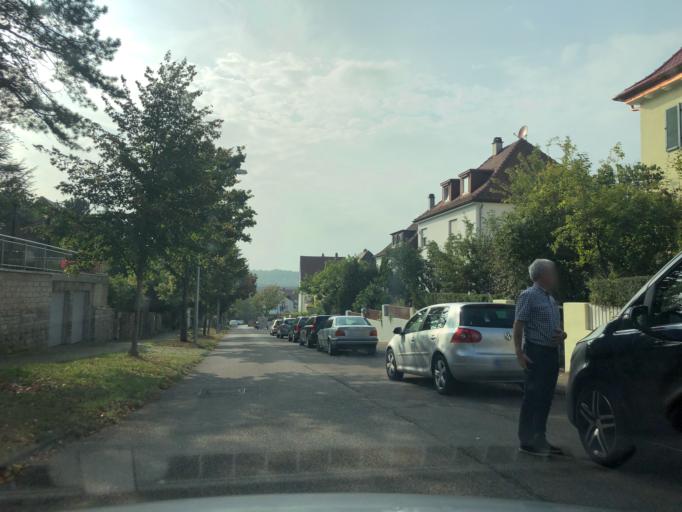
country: DE
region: Baden-Wuerttemberg
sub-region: Regierungsbezirk Stuttgart
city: Stuttgart Feuerbach
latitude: 48.8270
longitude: 9.1833
